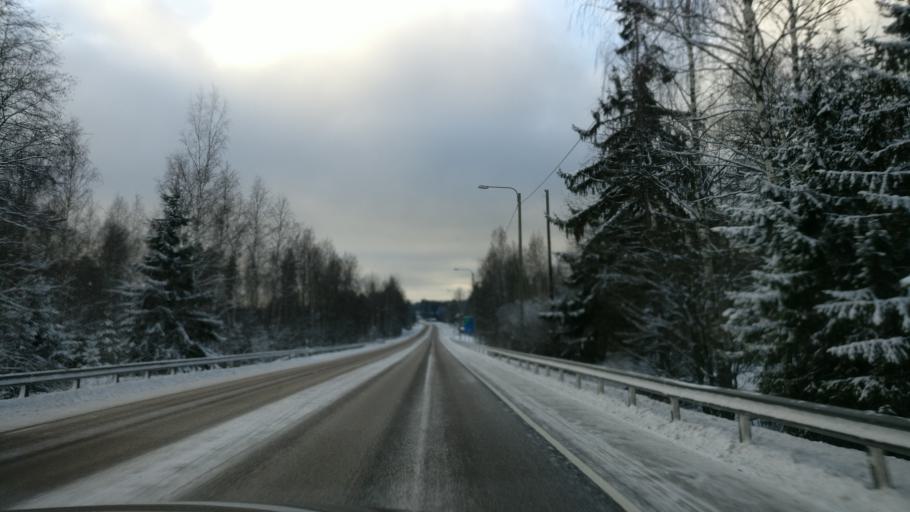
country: FI
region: Paijanne Tavastia
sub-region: Lahti
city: Heinola
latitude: 61.3362
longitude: 26.1767
